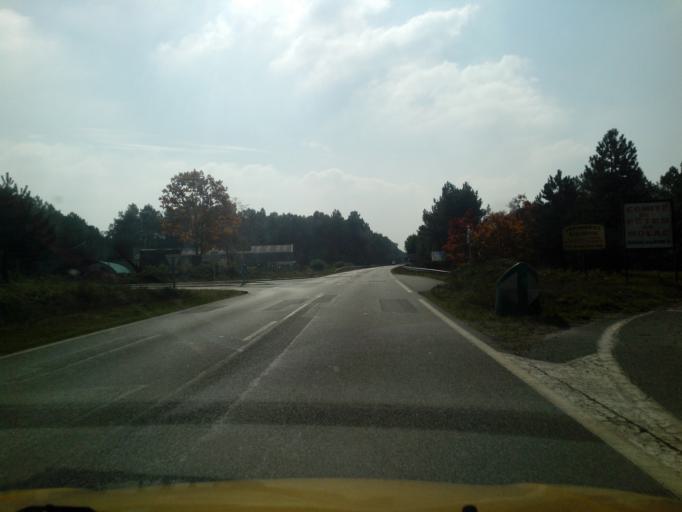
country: FR
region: Brittany
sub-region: Departement du Morbihan
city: Molac
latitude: 47.7442
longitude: -2.4372
